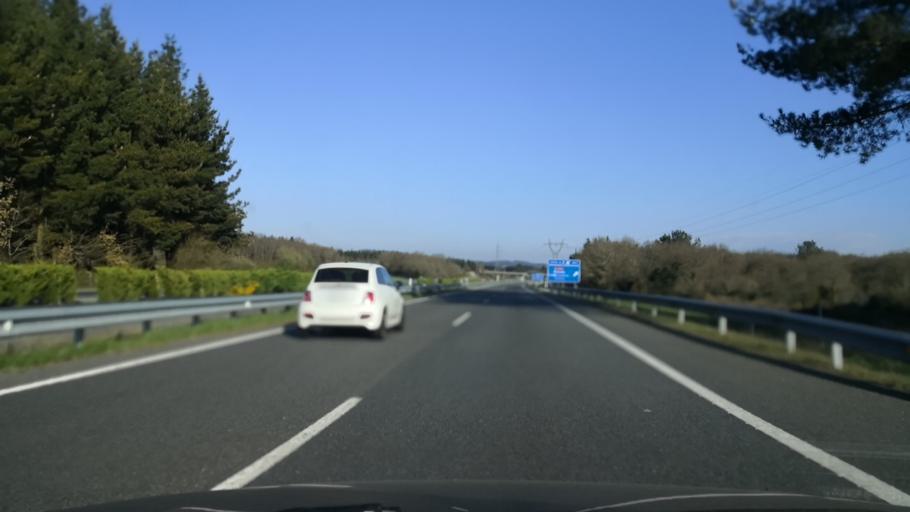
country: ES
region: Galicia
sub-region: Provincia de Lugo
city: Lugo
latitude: 43.0479
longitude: -7.5408
